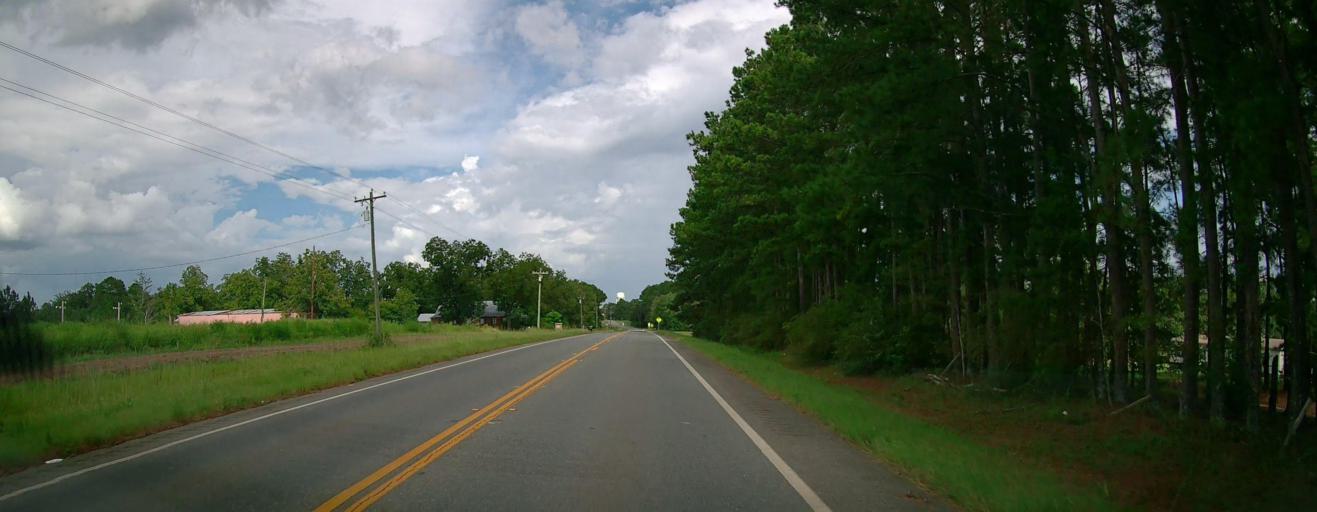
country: US
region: Georgia
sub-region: Coffee County
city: Douglas
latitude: 31.5387
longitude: -82.8730
